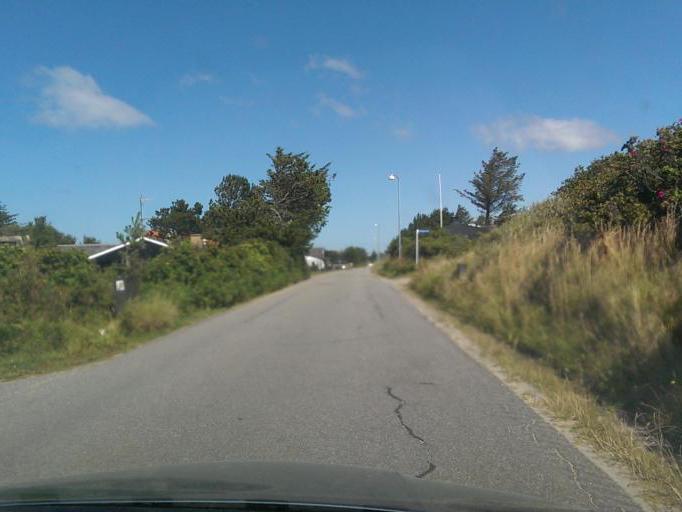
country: DK
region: North Denmark
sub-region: Jammerbugt Kommune
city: Pandrup
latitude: 57.2517
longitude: 9.5913
